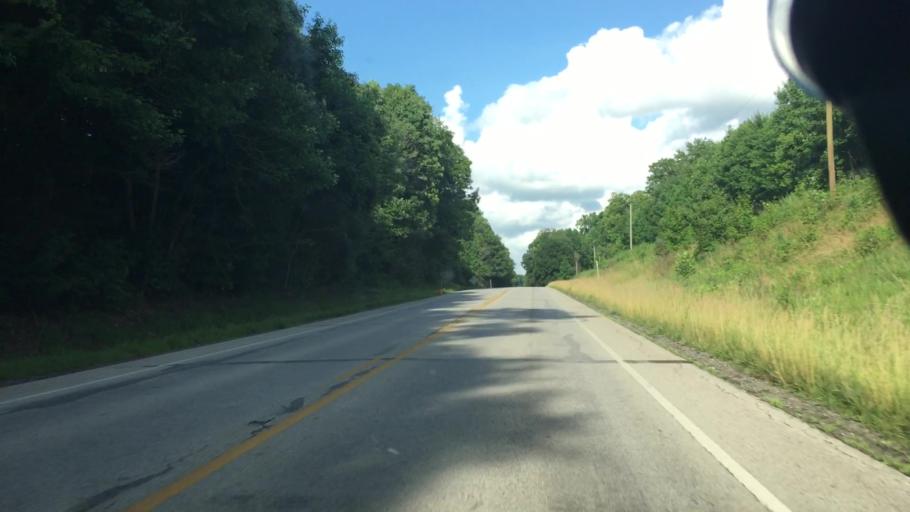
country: US
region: Kentucky
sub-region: Hancock County
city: Lewisport
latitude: 38.0013
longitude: -86.8519
